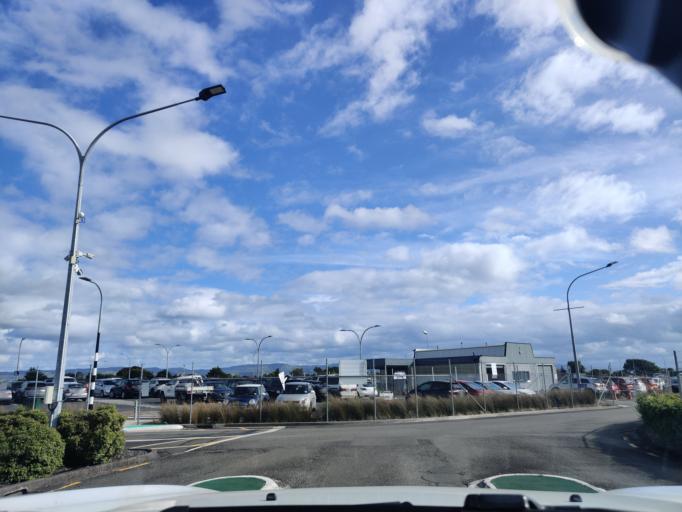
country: NZ
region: Manawatu-Wanganui
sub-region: Palmerston North City
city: Palmerston North
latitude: -40.3242
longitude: 175.6220
